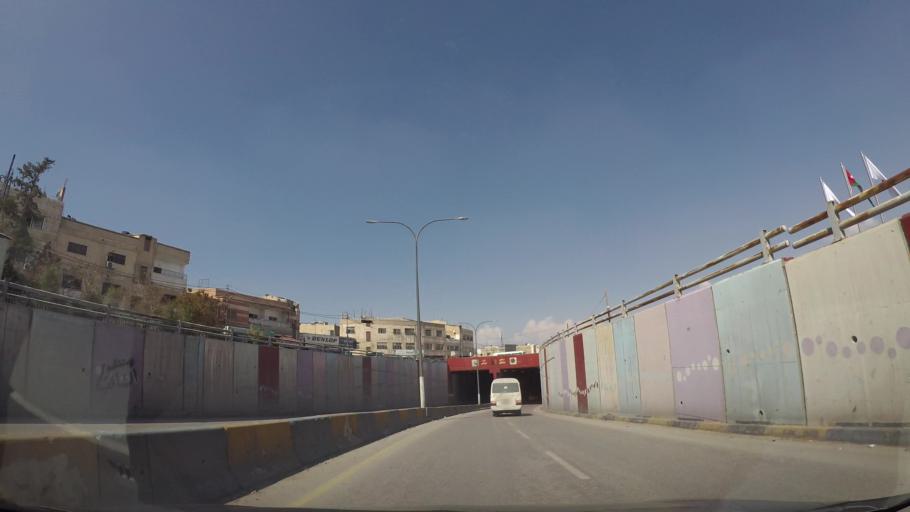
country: JO
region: Zarqa
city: Zarqa
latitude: 32.0715
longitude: 36.0982
